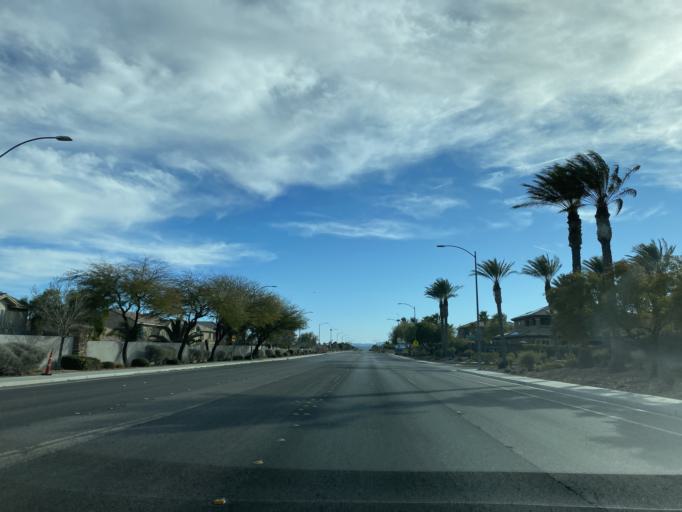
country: US
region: Nevada
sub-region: Clark County
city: Summerlin South
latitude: 36.2973
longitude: -115.3059
